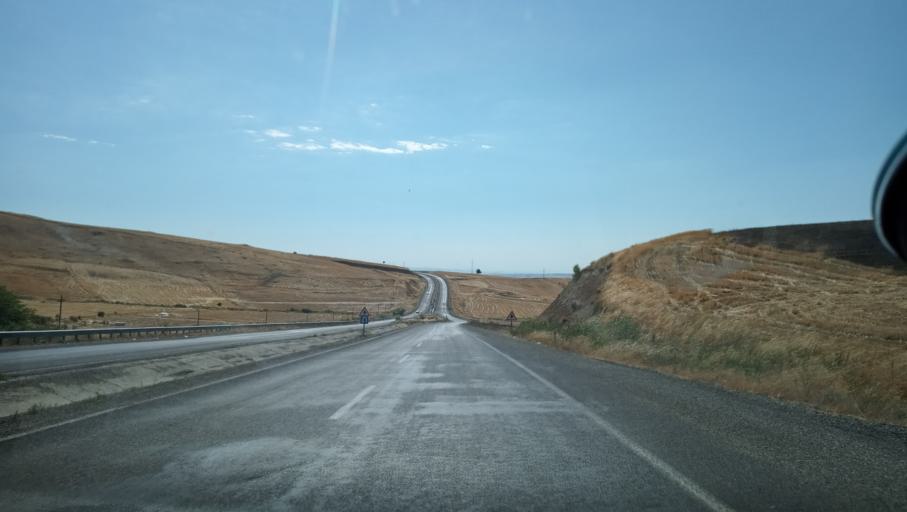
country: TR
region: Diyarbakir
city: Silvan
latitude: 38.1184
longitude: 41.1029
